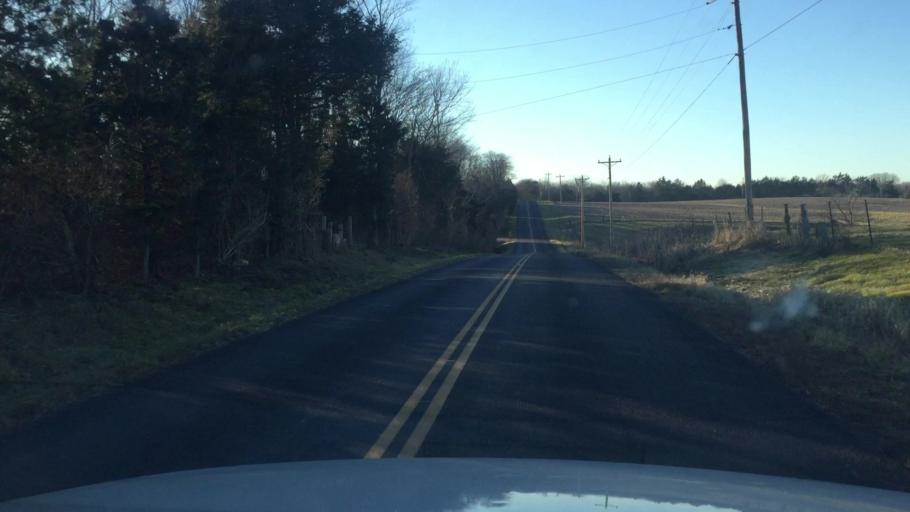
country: US
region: Missouri
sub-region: Boone County
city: Ashland
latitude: 38.8149
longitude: -92.2879
